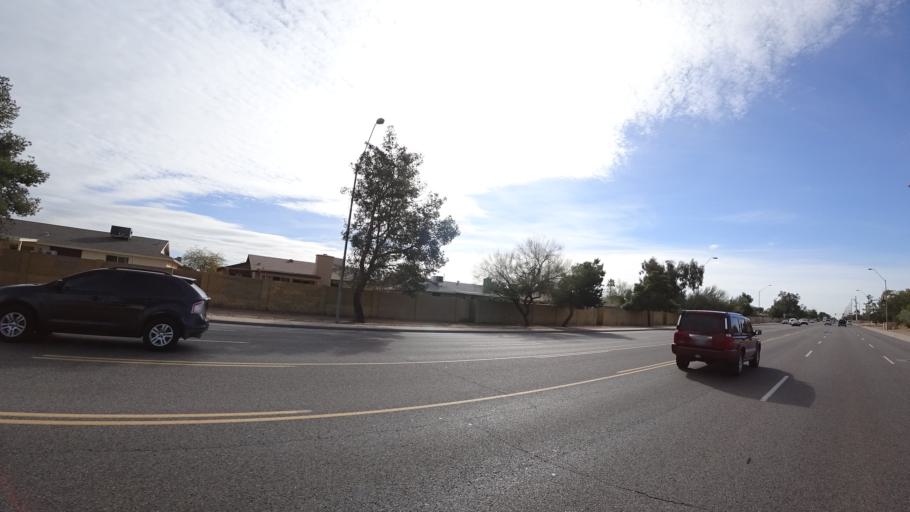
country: US
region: Arizona
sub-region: Maricopa County
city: Glendale
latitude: 33.6066
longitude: -112.1515
